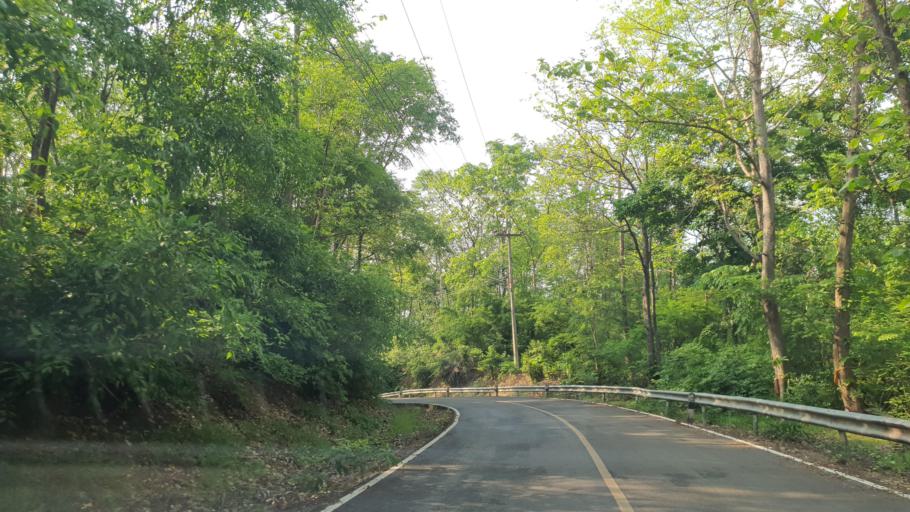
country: TH
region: Chiang Mai
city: Mae Wang
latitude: 18.6940
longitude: 98.8123
